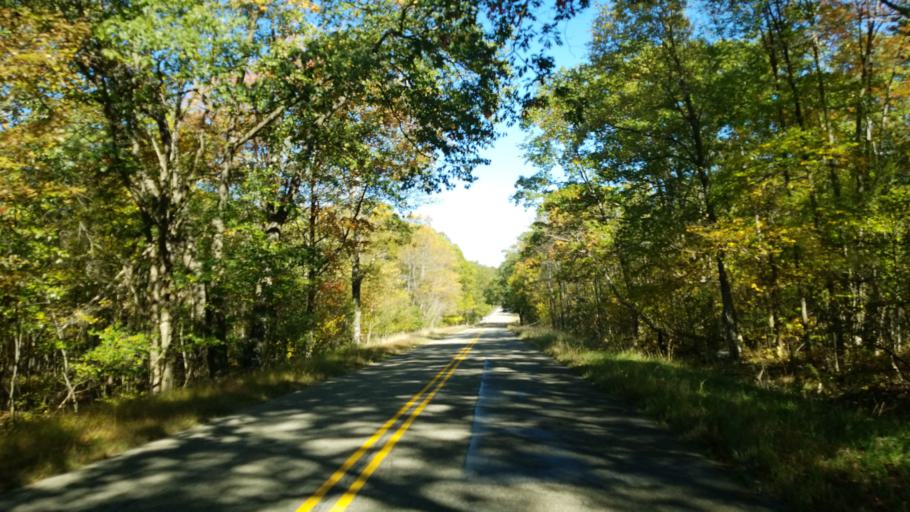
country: US
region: Pennsylvania
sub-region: Clearfield County
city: Shiloh
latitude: 41.2540
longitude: -78.3317
